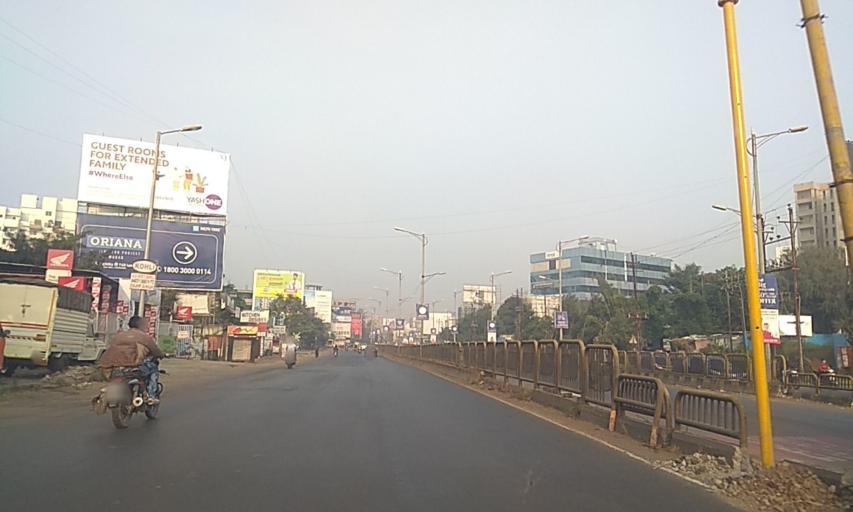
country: IN
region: Maharashtra
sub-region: Pune Division
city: Pimpri
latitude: 18.5903
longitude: 73.7684
